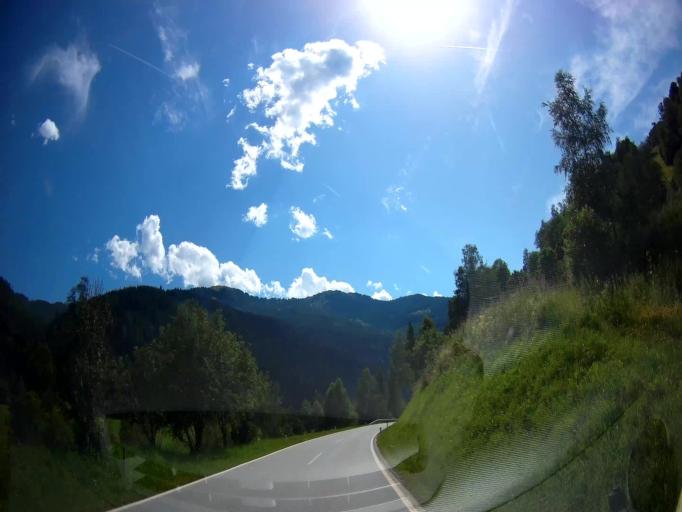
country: AT
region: Salzburg
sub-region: Politischer Bezirk Tamsweg
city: Ramingstein
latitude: 47.0663
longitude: 13.7936
